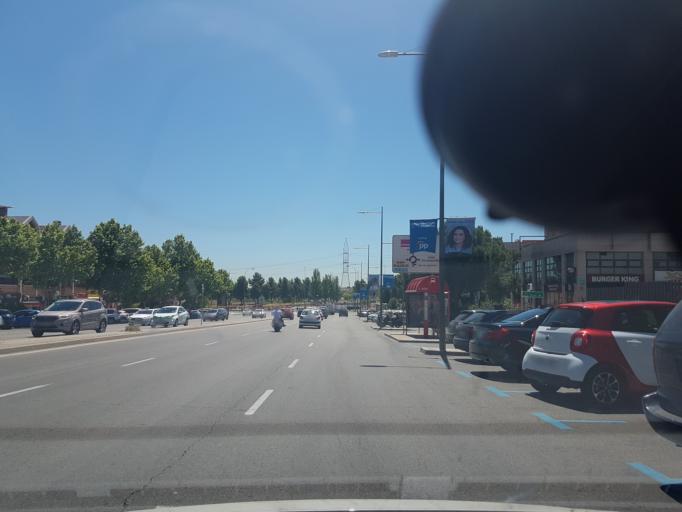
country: ES
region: Madrid
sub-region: Provincia de Madrid
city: Pozuelo de Alarcon
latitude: 40.4352
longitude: -3.7985
